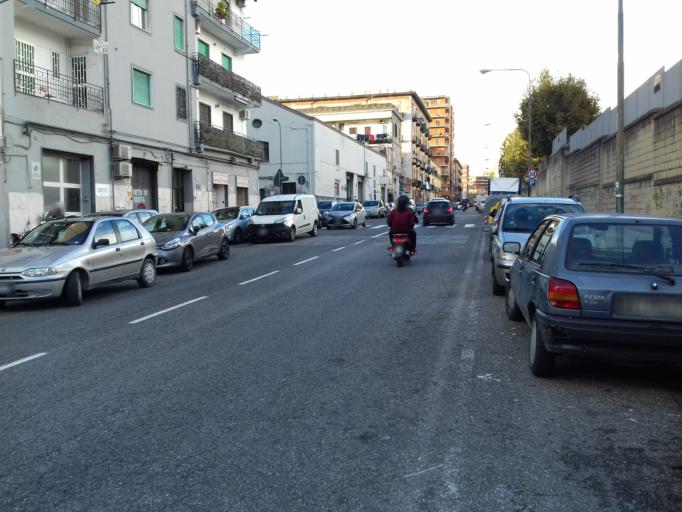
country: IT
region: Campania
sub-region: Provincia di Napoli
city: Napoli
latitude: 40.8608
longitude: 14.2733
